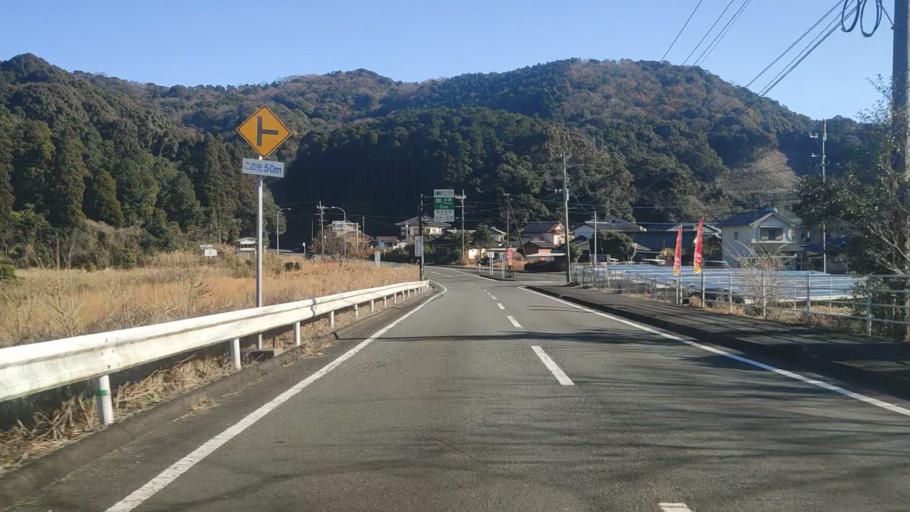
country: JP
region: Miyazaki
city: Nobeoka
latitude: 32.6882
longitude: 131.8071
